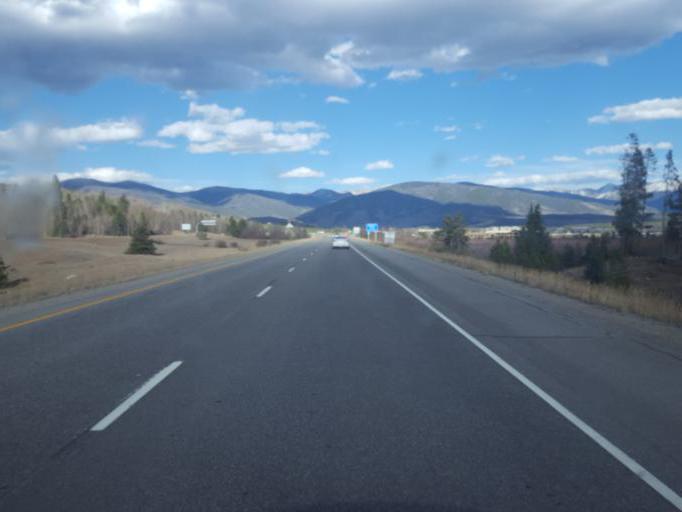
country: US
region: Colorado
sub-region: Summit County
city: Frisco
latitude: 39.5855
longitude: -106.1075
